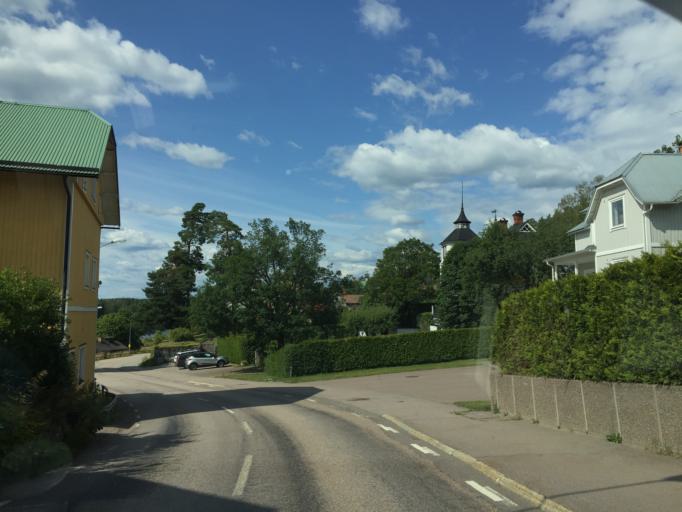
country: SE
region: Vaestmanland
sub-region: Norbergs Kommun
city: Norberg
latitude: 59.9567
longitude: 16.0113
